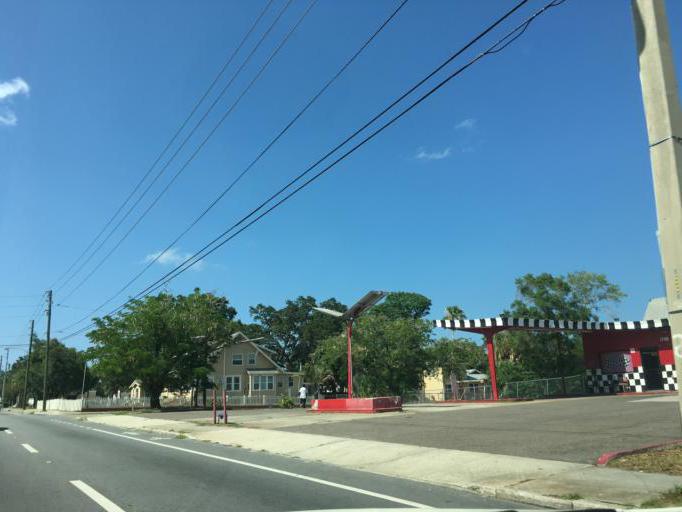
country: US
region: Florida
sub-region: Pinellas County
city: Saint Petersburg
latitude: 27.7530
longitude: -82.6466
